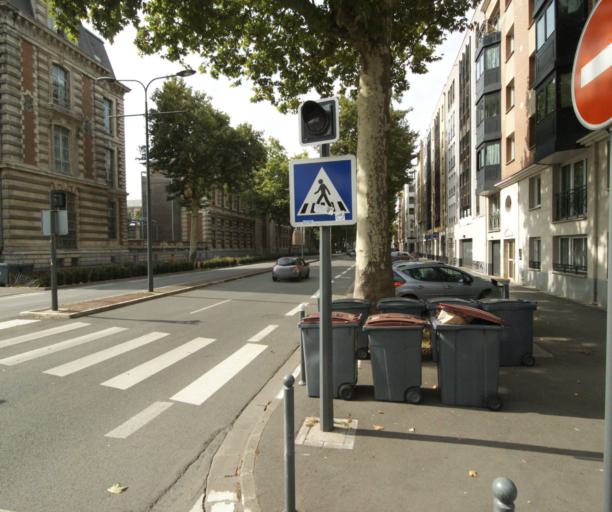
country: FR
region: Nord-Pas-de-Calais
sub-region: Departement du Nord
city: Lille
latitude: 50.6196
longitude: 3.0486
